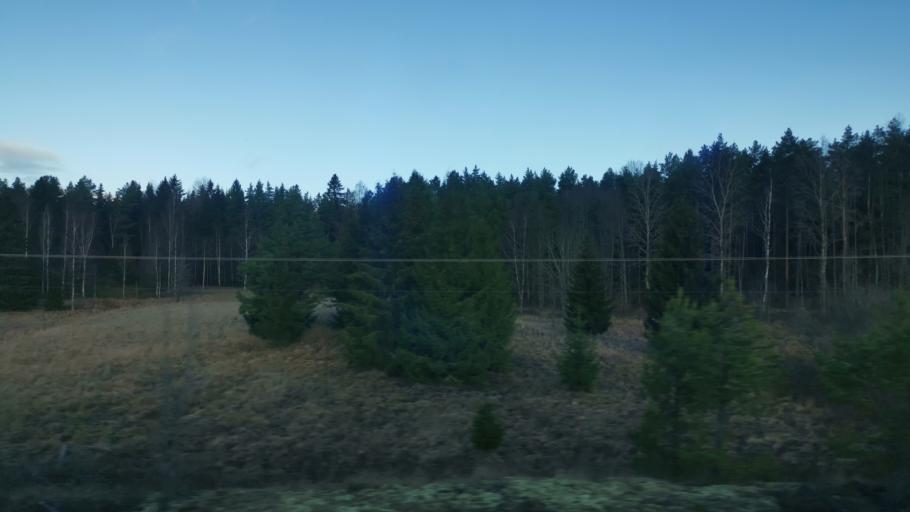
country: SE
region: Soedermanland
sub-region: Flens Kommun
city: Malmkoping
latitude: 59.0676
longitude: 16.7595
